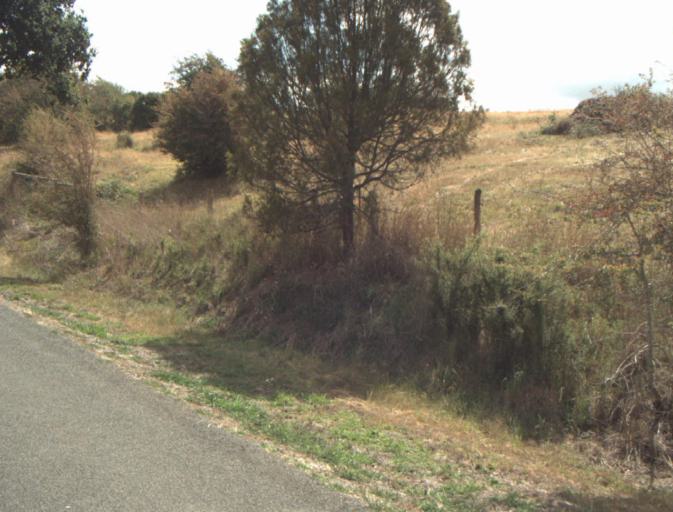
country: AU
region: Tasmania
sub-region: Launceston
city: Mayfield
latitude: -41.3151
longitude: 147.0062
